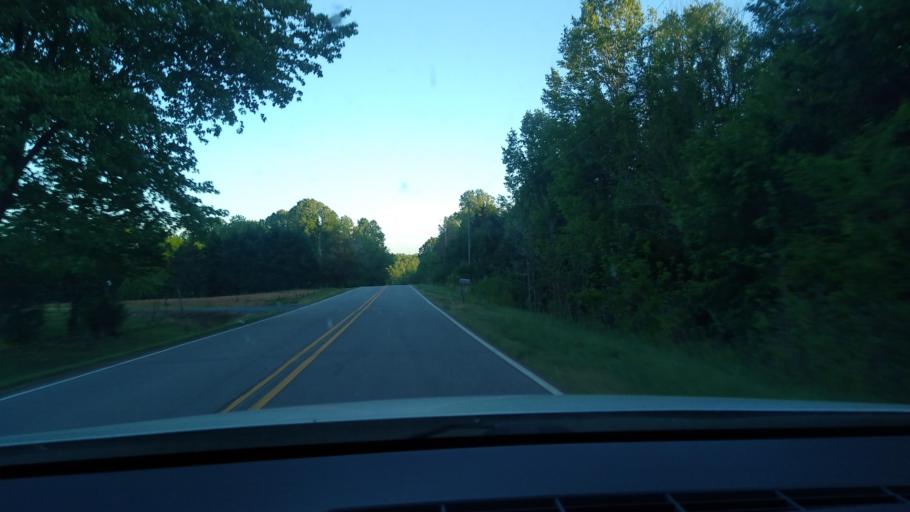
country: US
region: North Carolina
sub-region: Rockingham County
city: Reidsville
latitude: 36.3812
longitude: -79.5539
